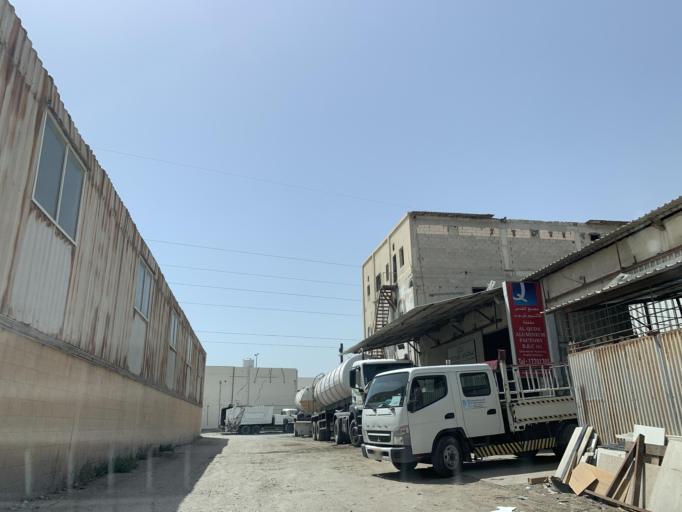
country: BH
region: Northern
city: Sitrah
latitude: 26.1378
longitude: 50.6072
